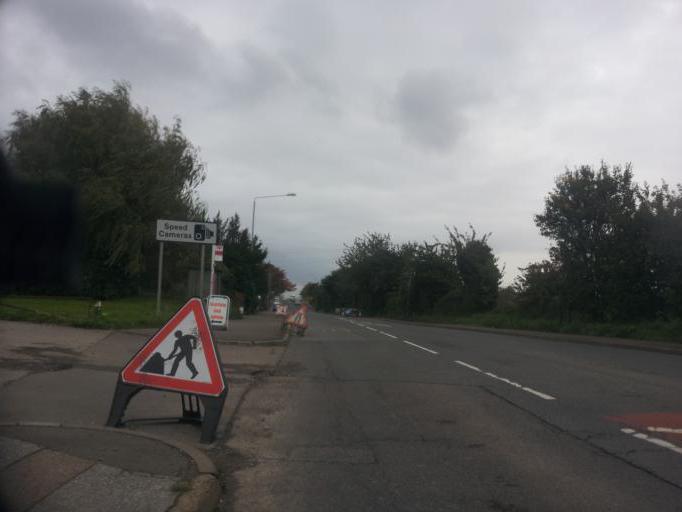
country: GB
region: England
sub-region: Kent
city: Sittingbourne
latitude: 51.3349
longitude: 0.7657
